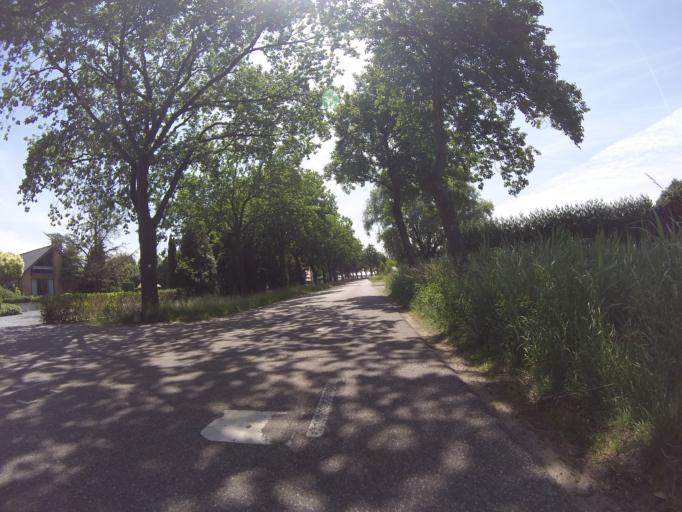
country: NL
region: Utrecht
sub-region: Gemeente Utrechtse Heuvelrug
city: Overberg
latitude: 52.0756
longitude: 5.5010
